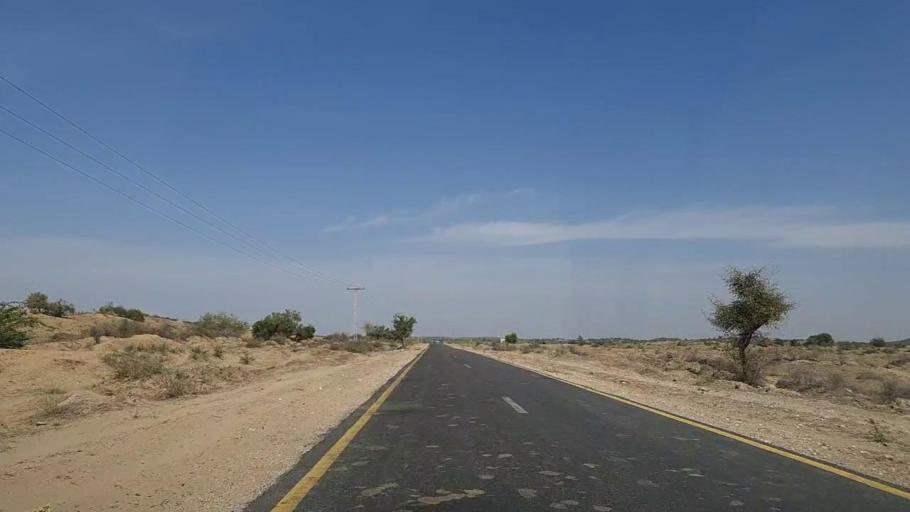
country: PK
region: Sindh
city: Mithi
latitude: 24.9588
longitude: 69.9073
